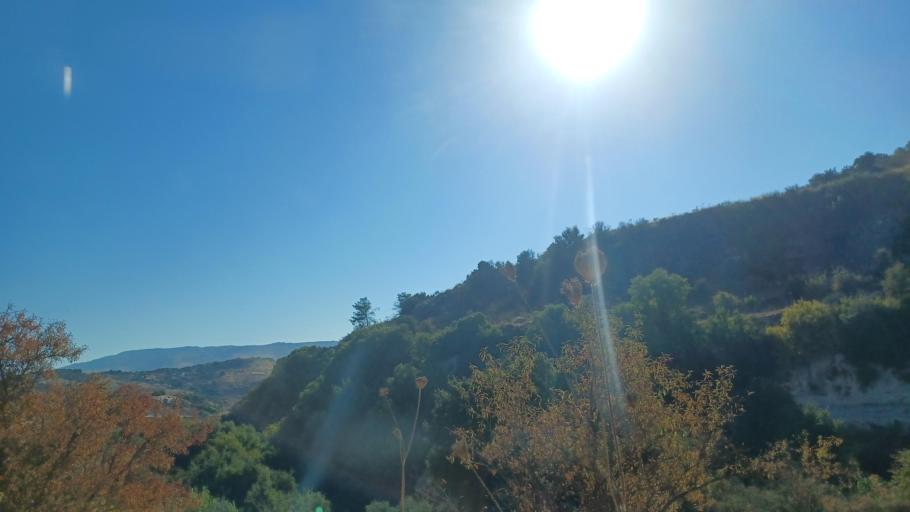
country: CY
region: Pafos
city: Mesogi
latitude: 34.8687
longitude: 32.5260
